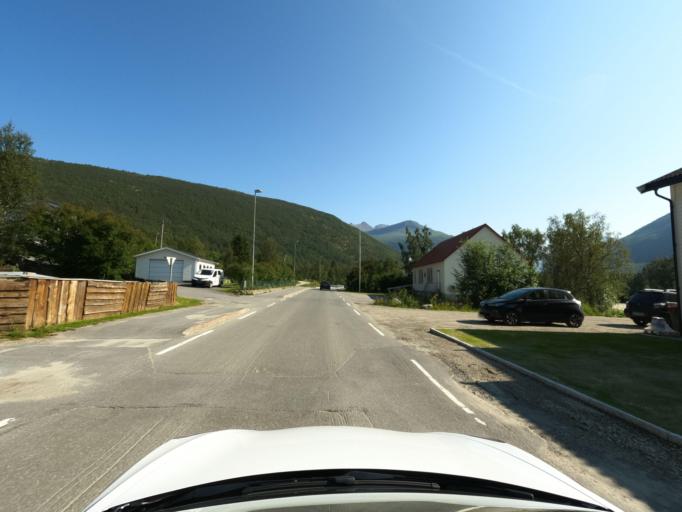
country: NO
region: Nordland
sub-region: Narvik
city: Bjerkvik
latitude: 68.3739
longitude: 17.6013
